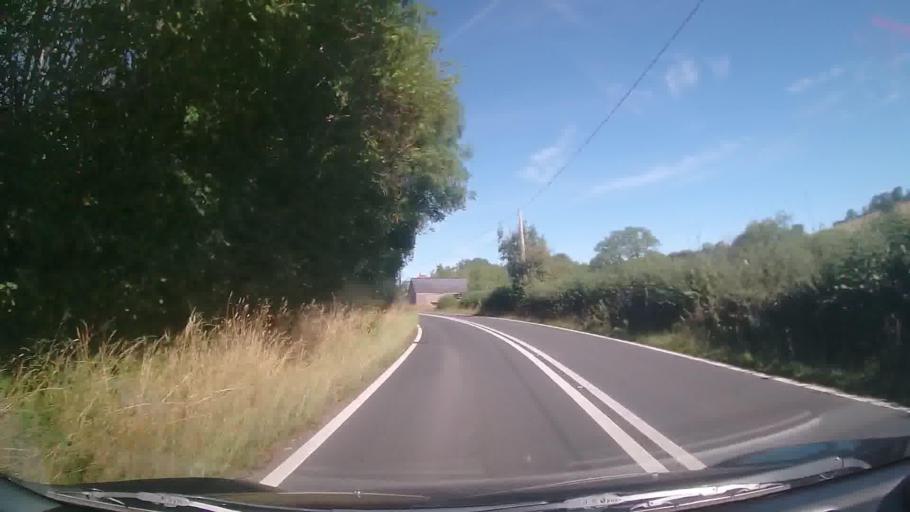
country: GB
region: Wales
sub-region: Sir Powys
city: Hay
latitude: 51.9580
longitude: -3.2029
